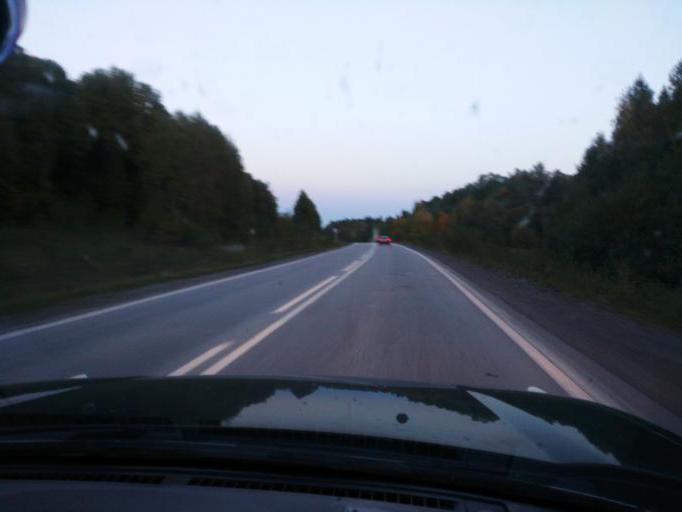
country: RU
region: Perm
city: Verkhnechusovskiye Gorodki
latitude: 58.2652
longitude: 56.9632
